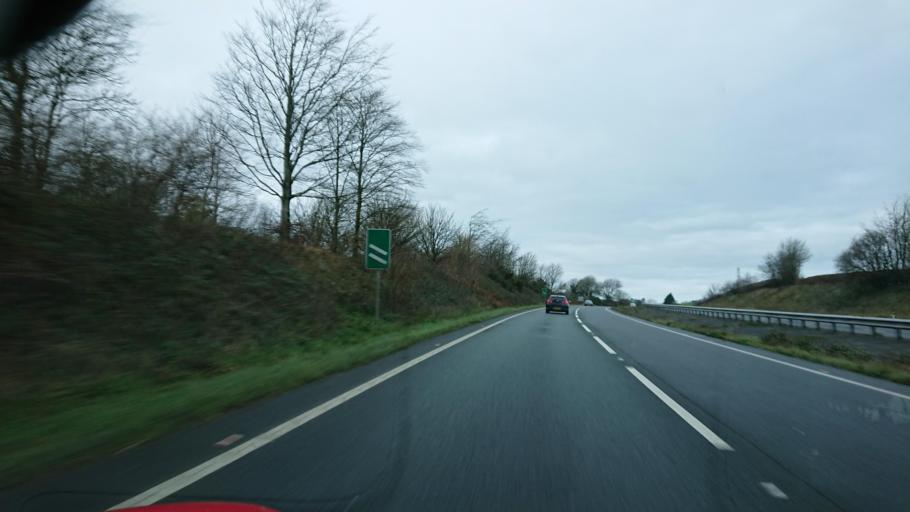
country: GB
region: England
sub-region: Cornwall
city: Liskeard
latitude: 50.4312
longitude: -4.4353
